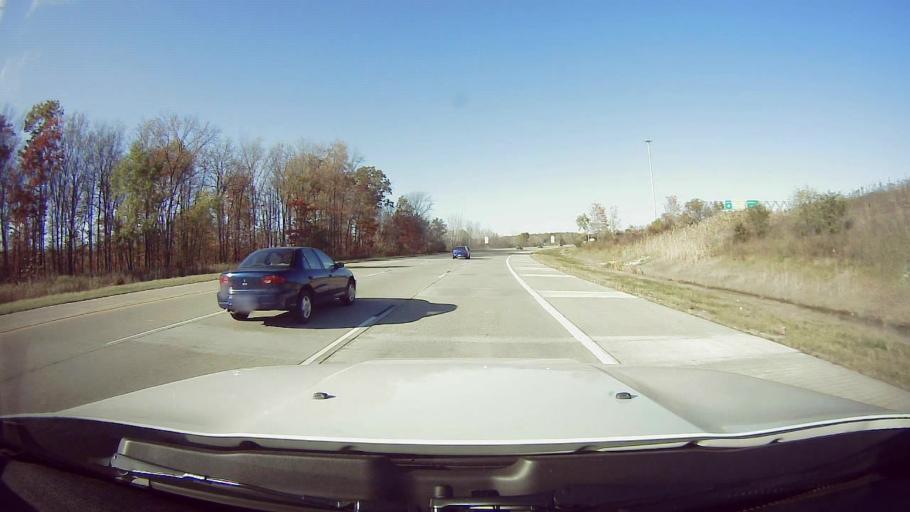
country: US
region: Michigan
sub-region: Oakland County
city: Novi
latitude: 42.4889
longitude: -83.4463
